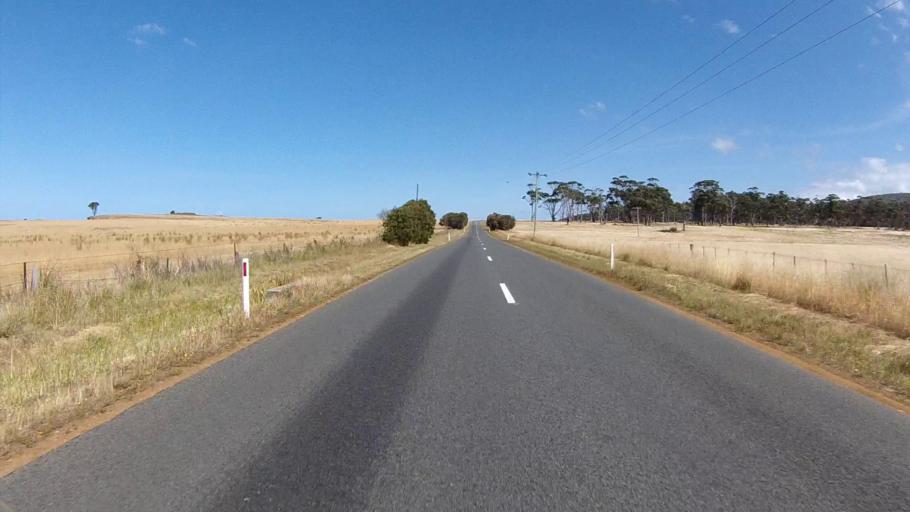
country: AU
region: Tasmania
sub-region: Sorell
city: Sorell
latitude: -42.2071
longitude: 148.0413
